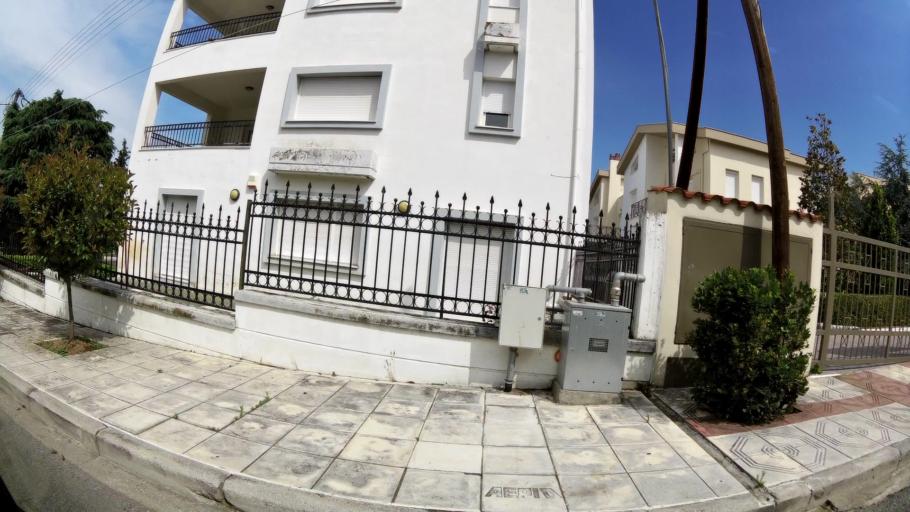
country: GR
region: Central Macedonia
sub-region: Nomos Thessalonikis
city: Panorama
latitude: 40.5789
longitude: 23.0141
